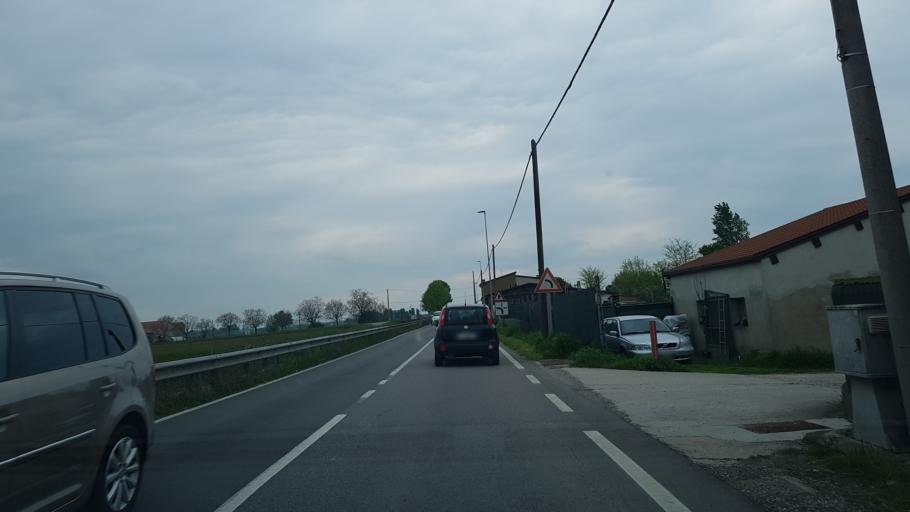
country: IT
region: Veneto
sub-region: Provincia di Verona
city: Cerea
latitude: 45.1541
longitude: 11.2296
